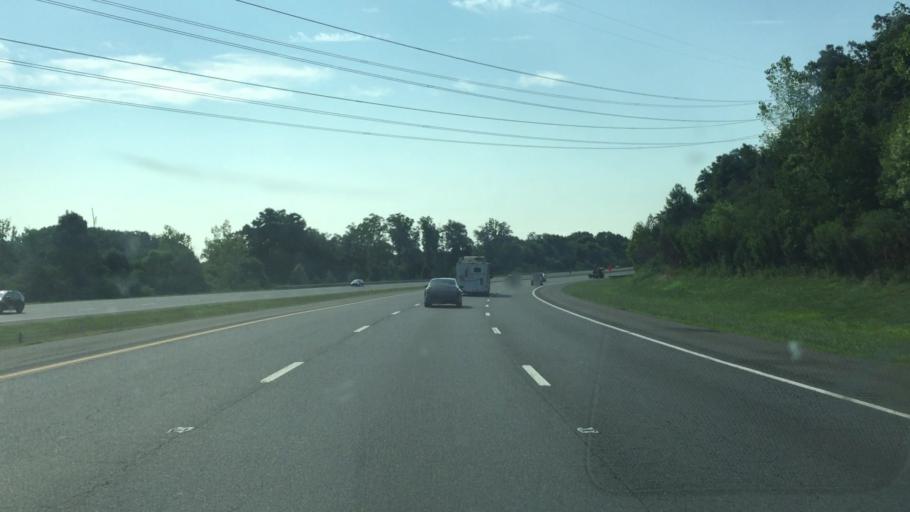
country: US
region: North Carolina
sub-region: Cabarrus County
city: Harrisburg
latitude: 35.3043
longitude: -80.6888
